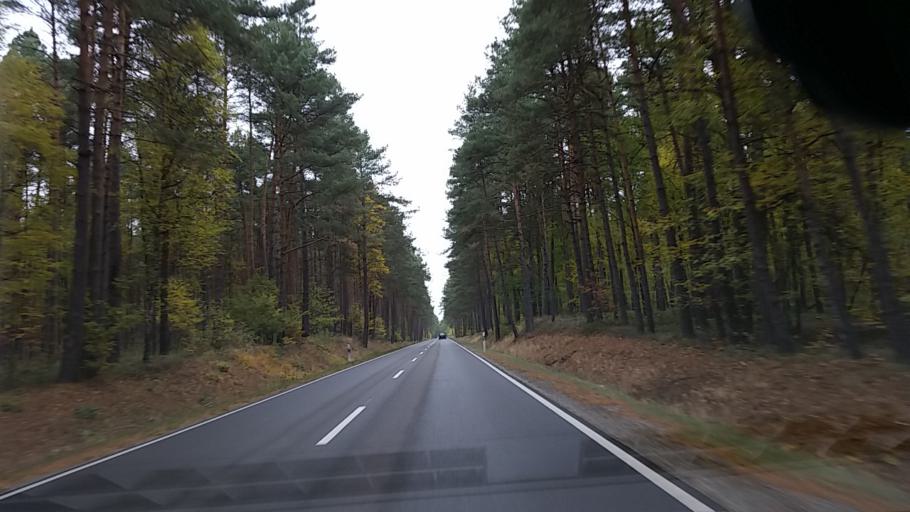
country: DE
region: Lower Saxony
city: Bergfeld
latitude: 52.6064
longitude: 10.8050
